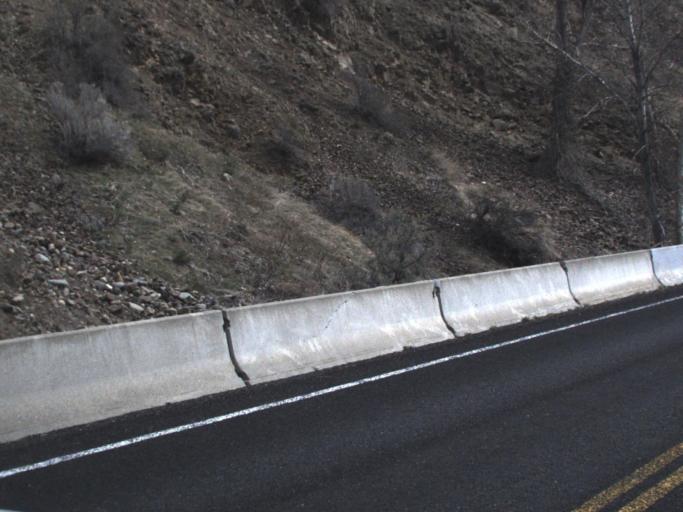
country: US
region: Washington
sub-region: Yakima County
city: Tieton
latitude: 46.7864
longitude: -120.8669
